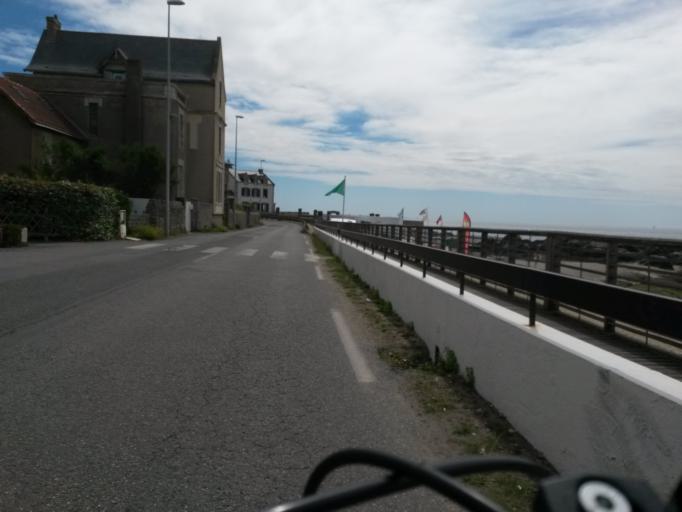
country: FR
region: Pays de la Loire
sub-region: Departement de la Loire-Atlantique
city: Le Croisic
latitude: 47.2839
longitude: -2.5126
